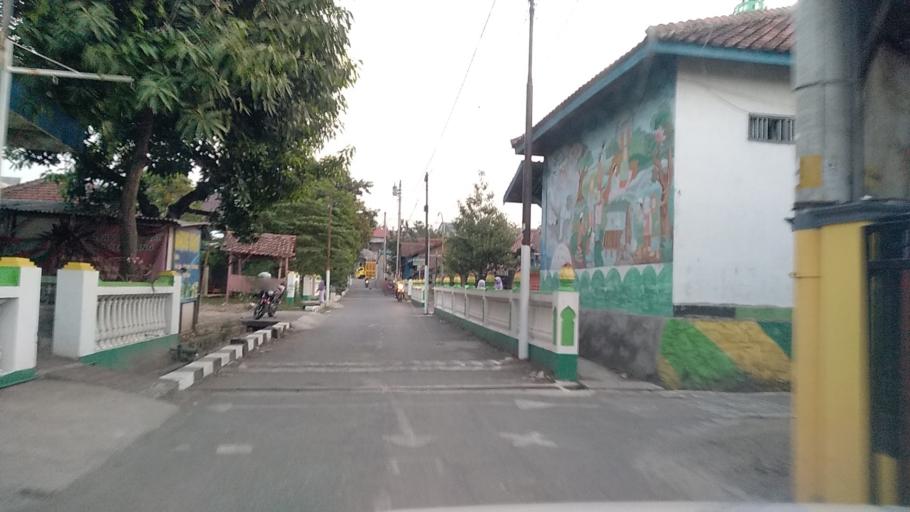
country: ID
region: Central Java
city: Semarang
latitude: -6.9743
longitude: 110.3187
